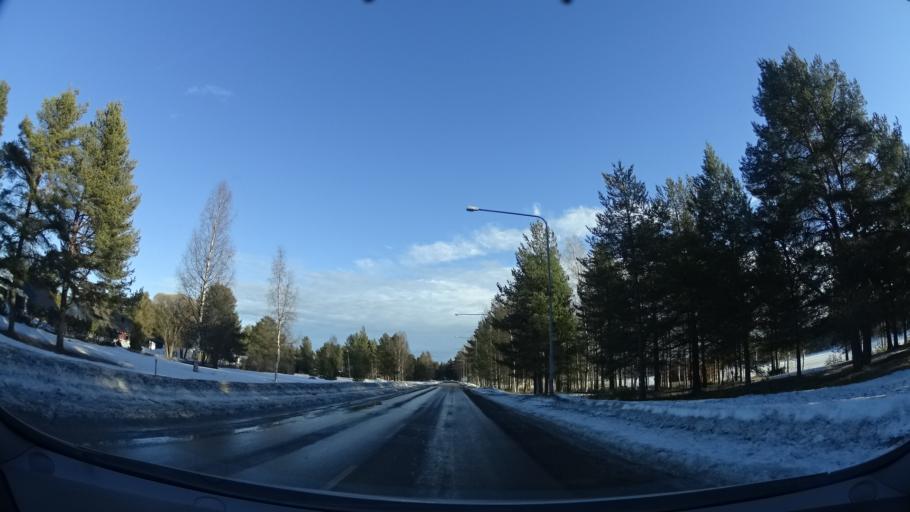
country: SE
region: Vaesterbotten
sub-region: Skelleftea Kommun
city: Byske
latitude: 64.9477
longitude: 21.2263
